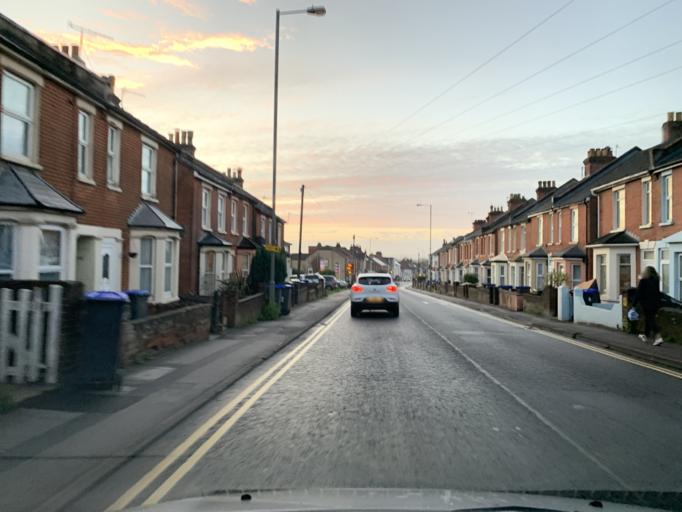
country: GB
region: England
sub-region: Wiltshire
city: Salisbury
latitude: 51.0765
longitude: -1.8100
